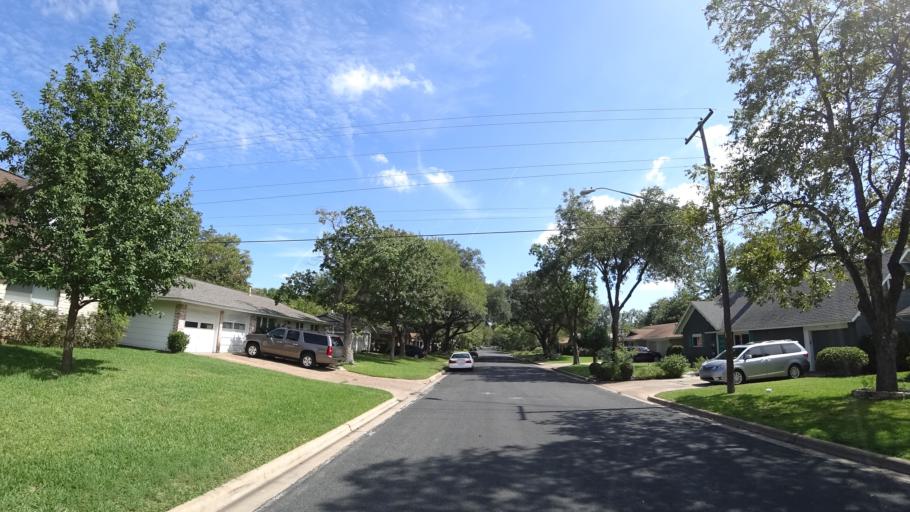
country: US
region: Texas
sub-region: Travis County
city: Austin
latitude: 30.3428
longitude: -97.7347
